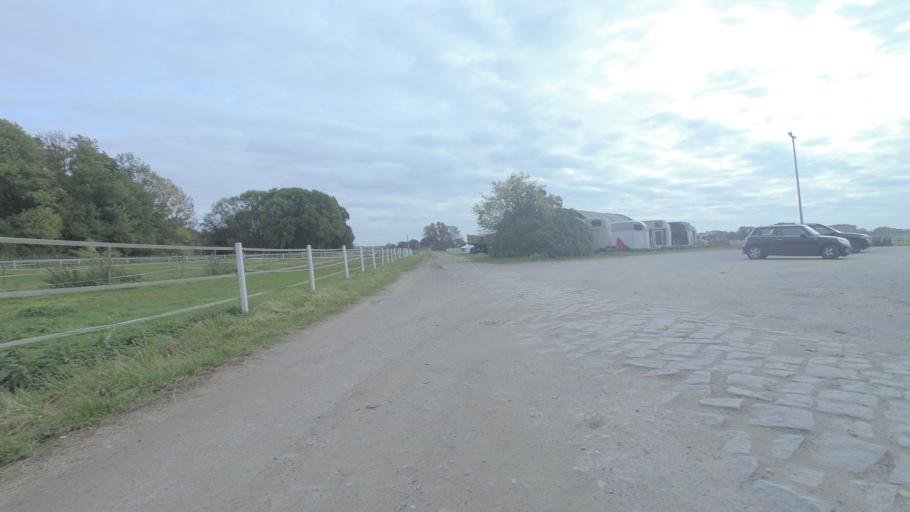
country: DE
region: Brandenburg
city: Grossbeeren
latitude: 52.3111
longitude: 13.3248
